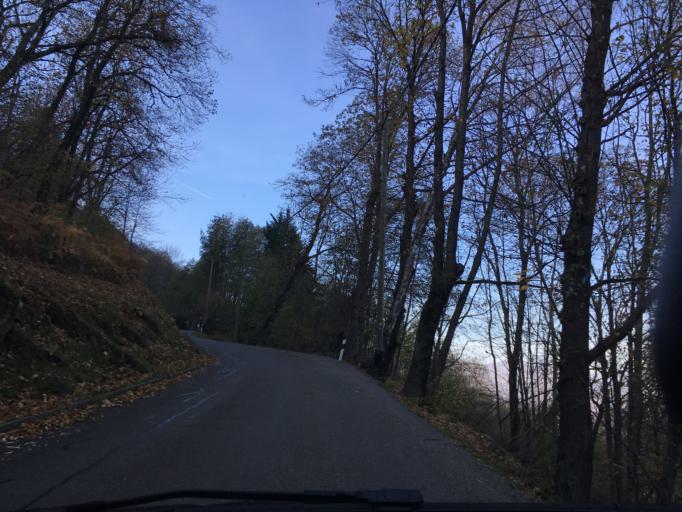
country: CH
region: Ticino
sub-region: Locarno District
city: Magadino
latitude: 46.1295
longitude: 8.8369
